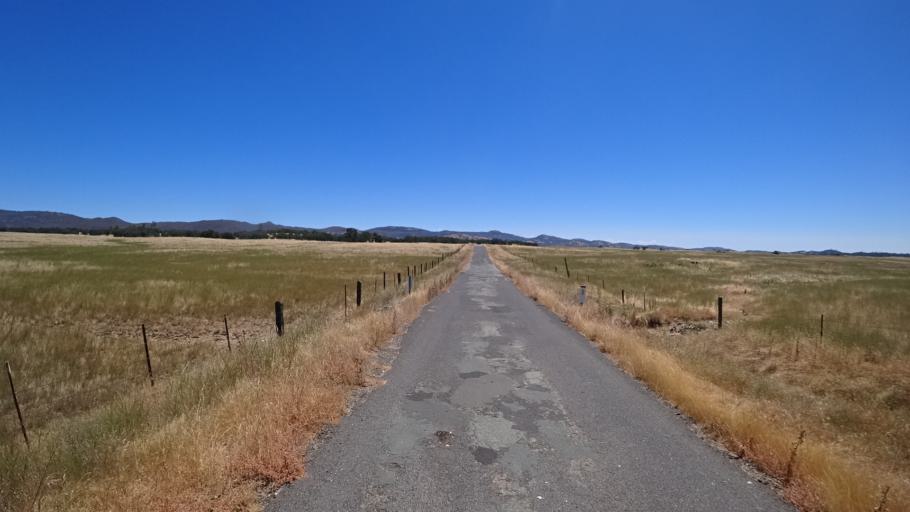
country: US
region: California
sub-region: Calaveras County
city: Rancho Calaveras
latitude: 38.0574
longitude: -120.7581
